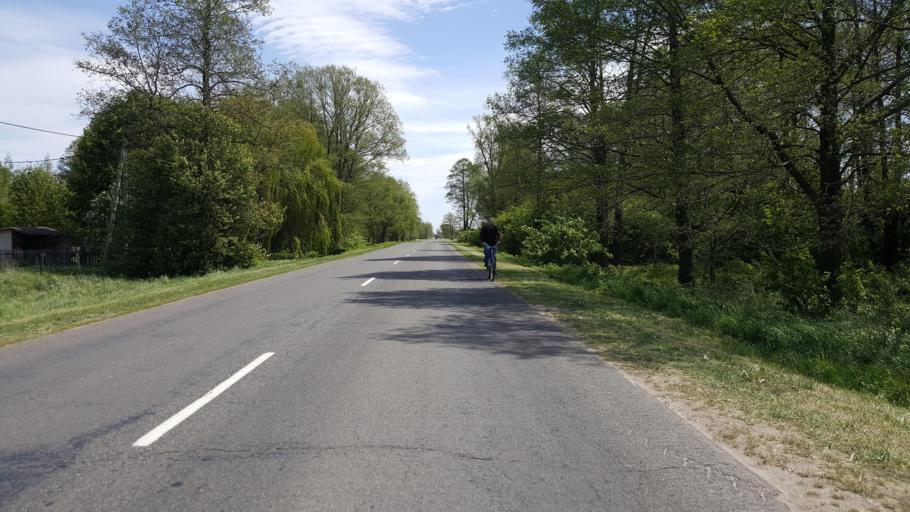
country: BY
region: Brest
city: Kobryn
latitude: 52.3454
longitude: 24.2178
